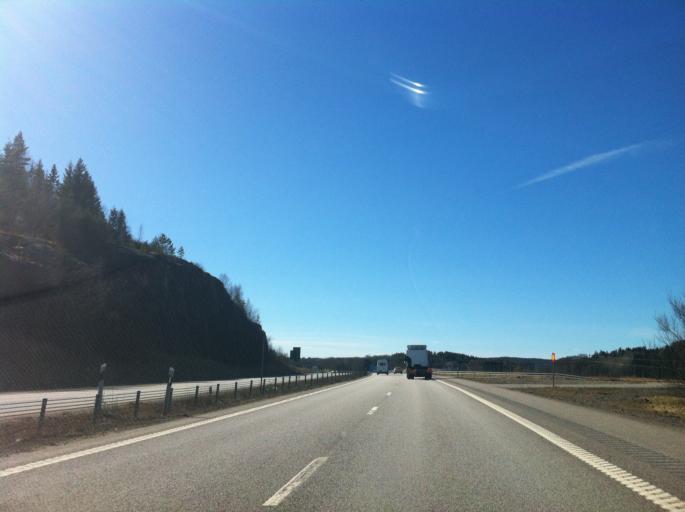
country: SE
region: Vaestra Goetaland
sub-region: Munkedals Kommun
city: Munkedal
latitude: 58.4093
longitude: 11.7353
